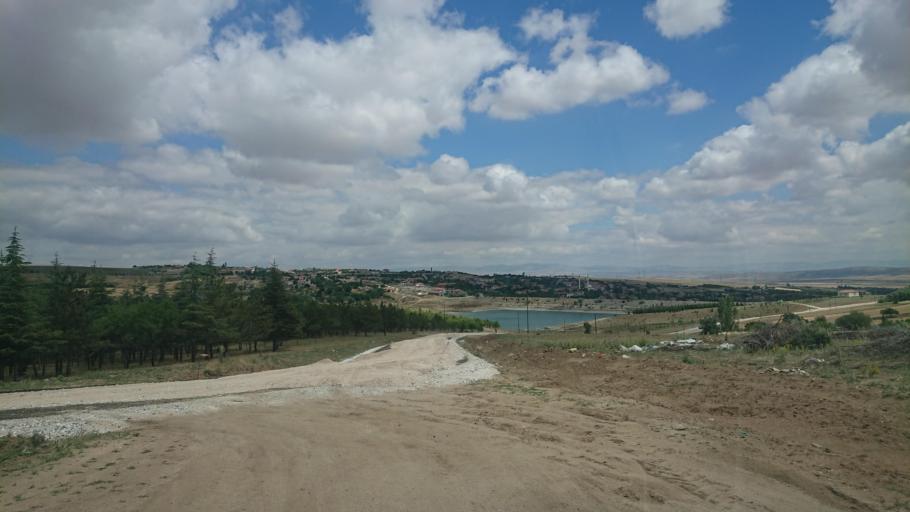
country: TR
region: Aksaray
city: Agacoren
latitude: 38.8593
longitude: 33.9479
